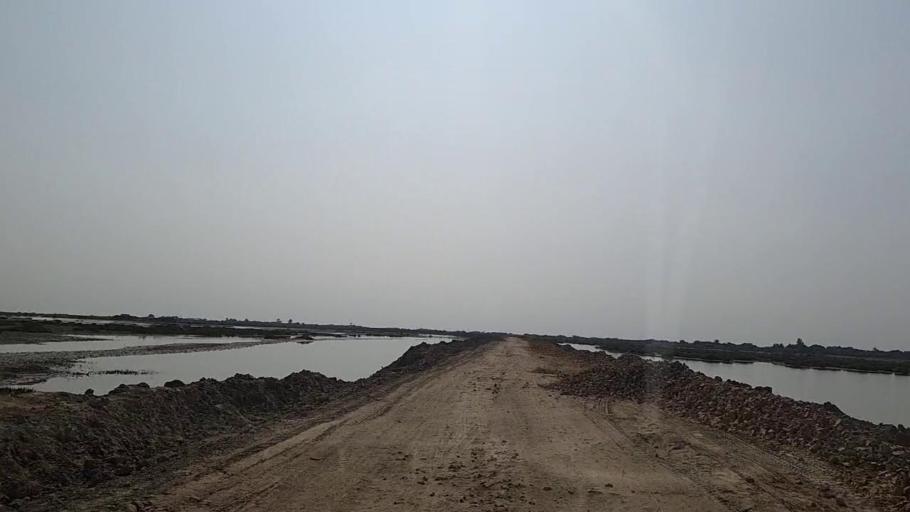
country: PK
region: Sindh
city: Chuhar Jamali
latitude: 24.2010
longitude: 67.8506
